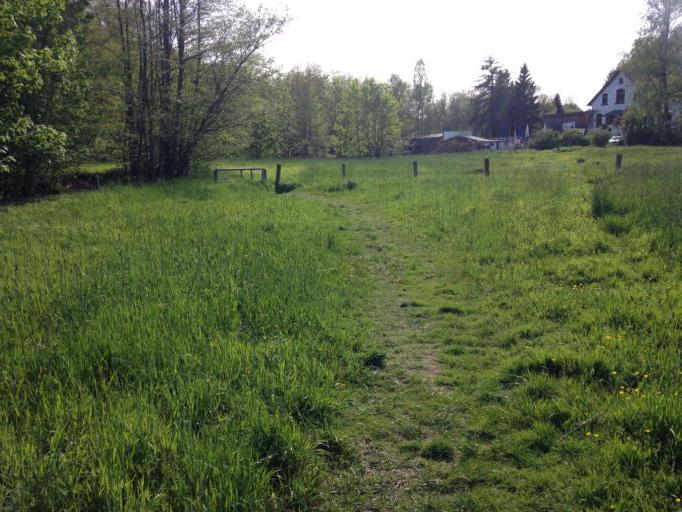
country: DE
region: North Rhine-Westphalia
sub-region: Regierungsbezirk Detmold
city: Lemgo
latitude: 52.0222
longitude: 8.9304
